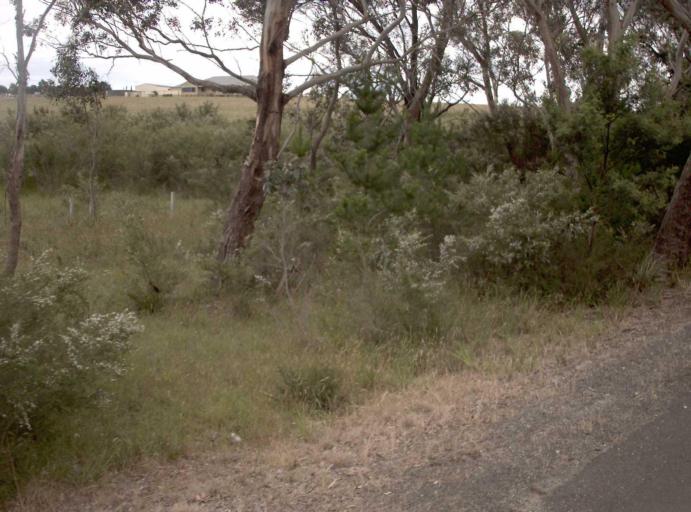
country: AU
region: Victoria
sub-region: Wellington
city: Sale
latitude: -38.2068
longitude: 147.0700
